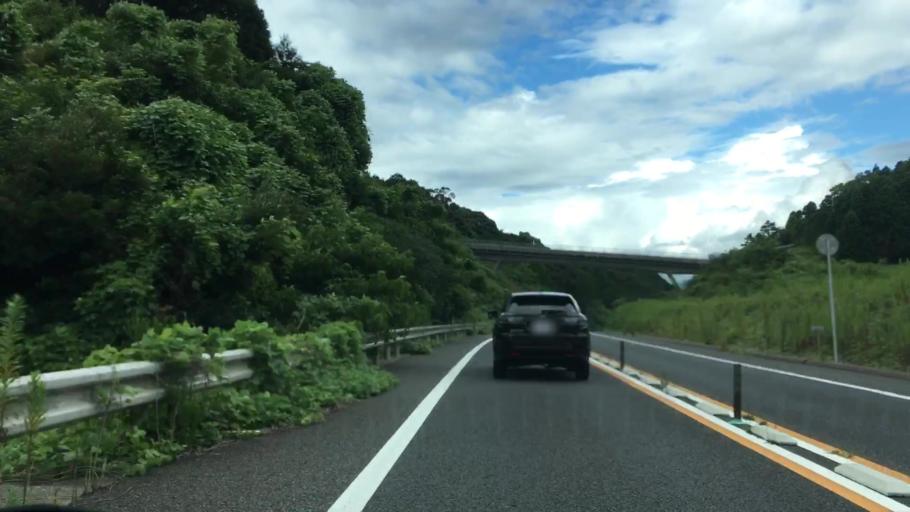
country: JP
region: Saga Prefecture
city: Karatsu
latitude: 33.3982
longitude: 129.9372
